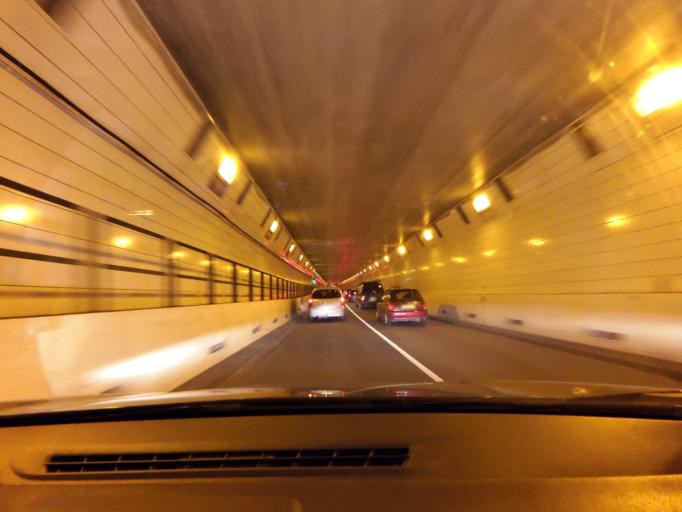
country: NL
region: South Holland
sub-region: Gemeente Rotterdam
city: Delfshaven
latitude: 51.9013
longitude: 4.4680
